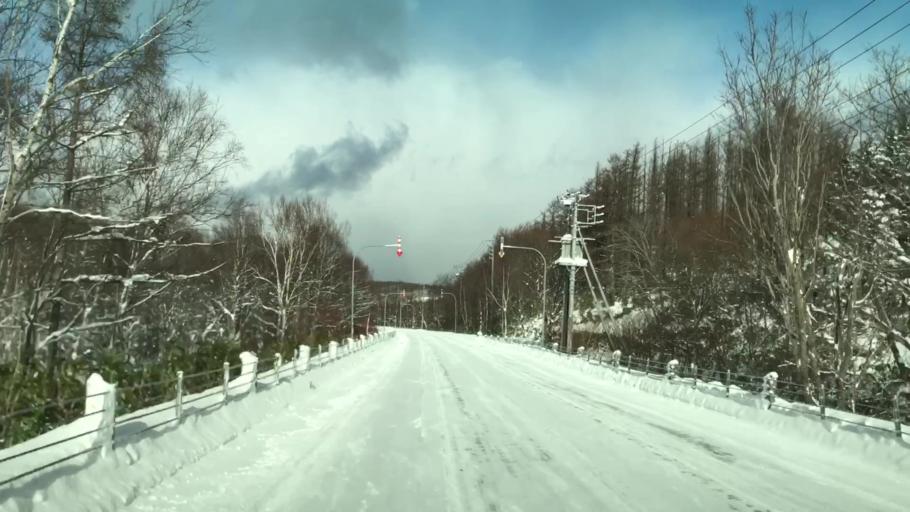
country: JP
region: Hokkaido
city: Yoichi
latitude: 43.2983
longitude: 140.5676
